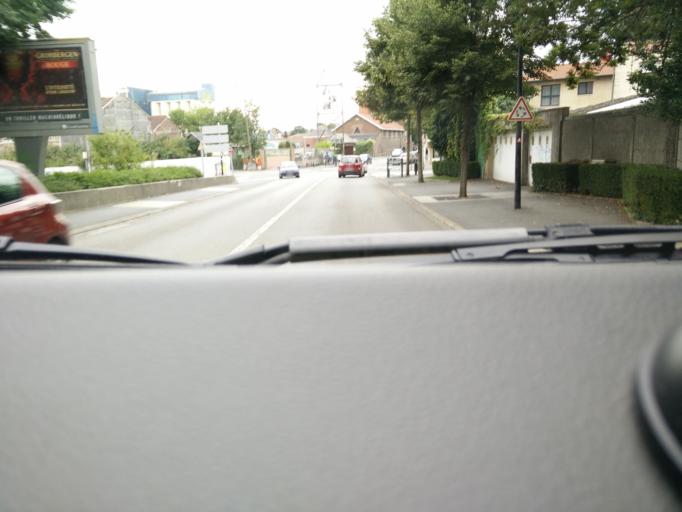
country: FR
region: Nord-Pas-de-Calais
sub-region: Departement du Nord
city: Valenciennes
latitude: 50.3533
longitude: 3.5150
